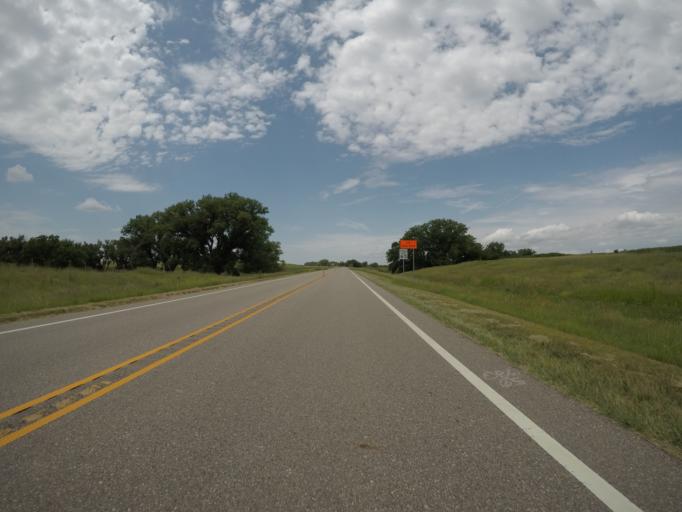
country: US
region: Kansas
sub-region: Graham County
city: Hill City
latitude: 39.3942
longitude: -99.6377
